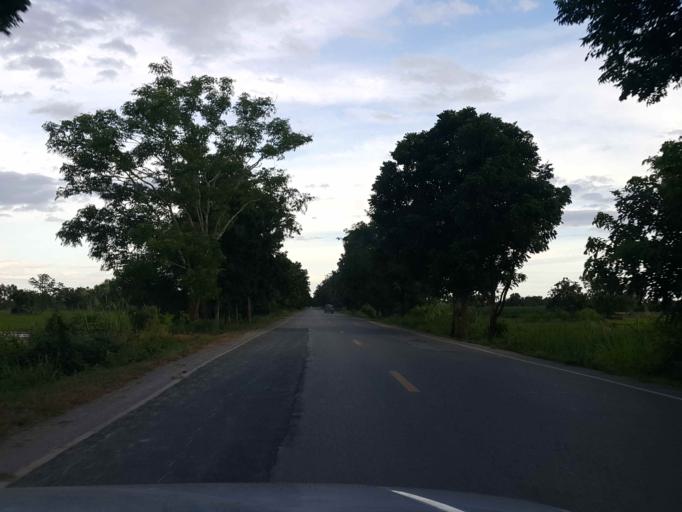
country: TH
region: Sukhothai
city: Sawankhalok
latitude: 17.3780
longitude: 99.7384
